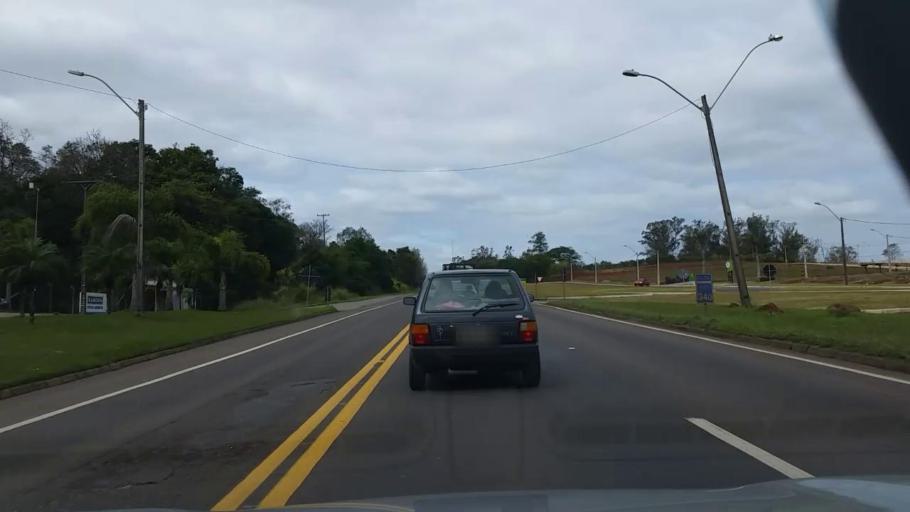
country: BR
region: Rio Grande do Sul
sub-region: Lajeado
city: Lajeado
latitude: -29.4289
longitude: -52.0166
